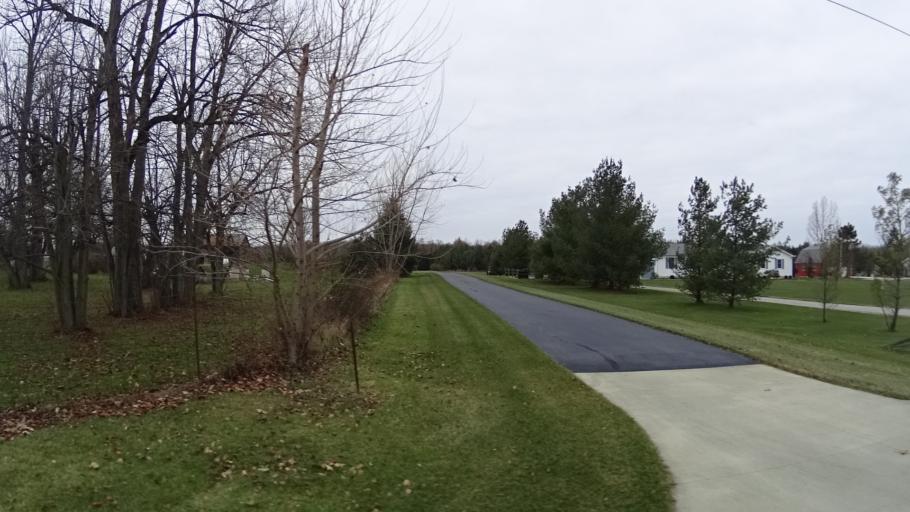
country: US
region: Ohio
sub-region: Lorain County
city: Wellington
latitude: 41.1427
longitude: -82.2692
